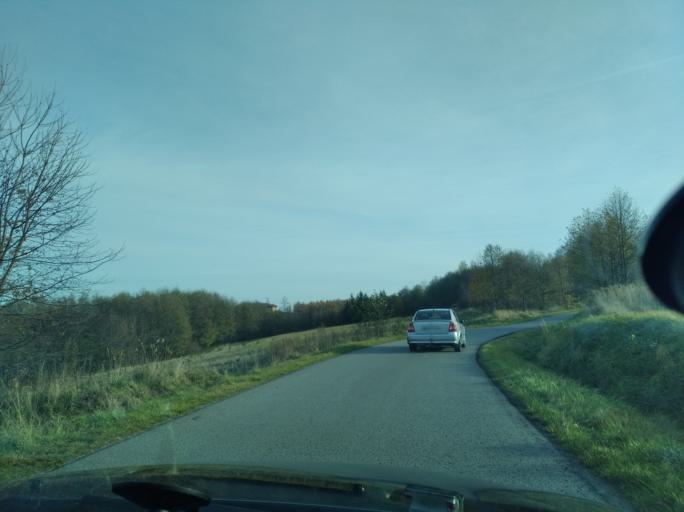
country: PL
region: Subcarpathian Voivodeship
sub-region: Powiat rzeszowski
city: Lubenia
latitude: 49.9349
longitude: 21.9348
